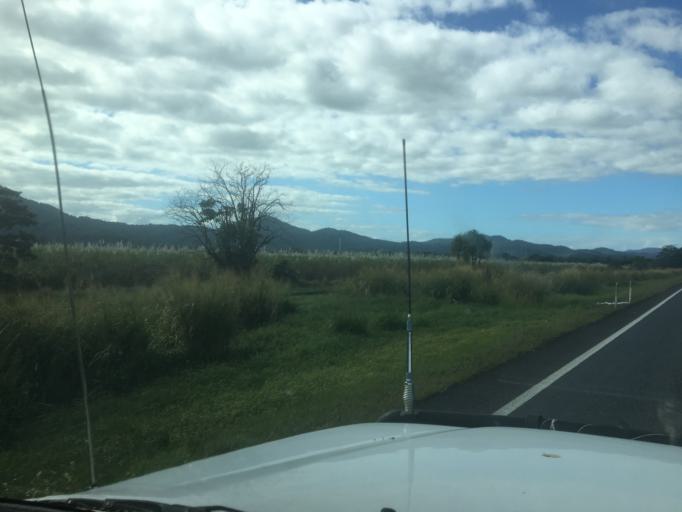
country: AU
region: Queensland
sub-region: Cassowary Coast
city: Innisfail
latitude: -17.2905
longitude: 145.9251
